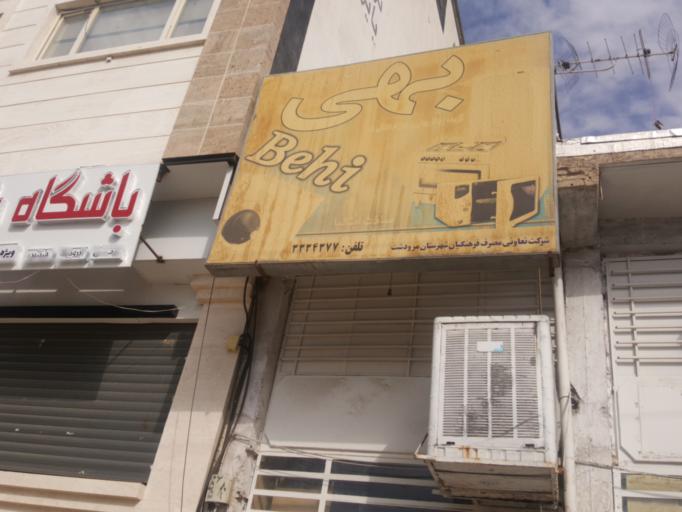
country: IR
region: Fars
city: Marvdasht
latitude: 29.8848
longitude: 52.8123
